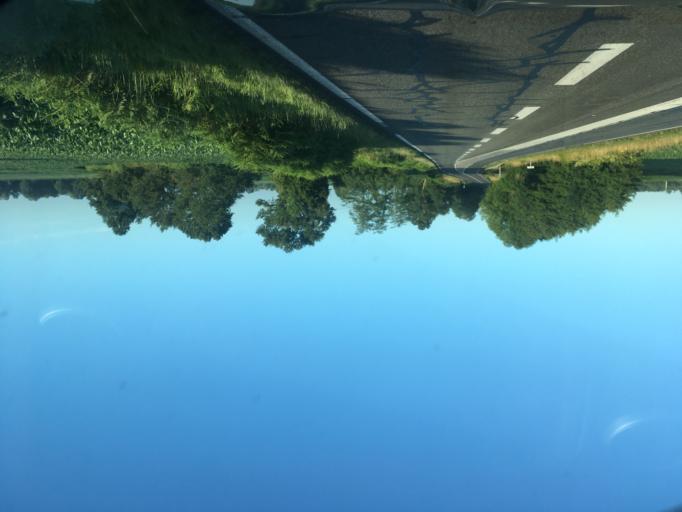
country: FR
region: Aquitaine
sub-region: Departement des Pyrenees-Atlantiques
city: Soumoulou
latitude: 43.2516
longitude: -0.1246
